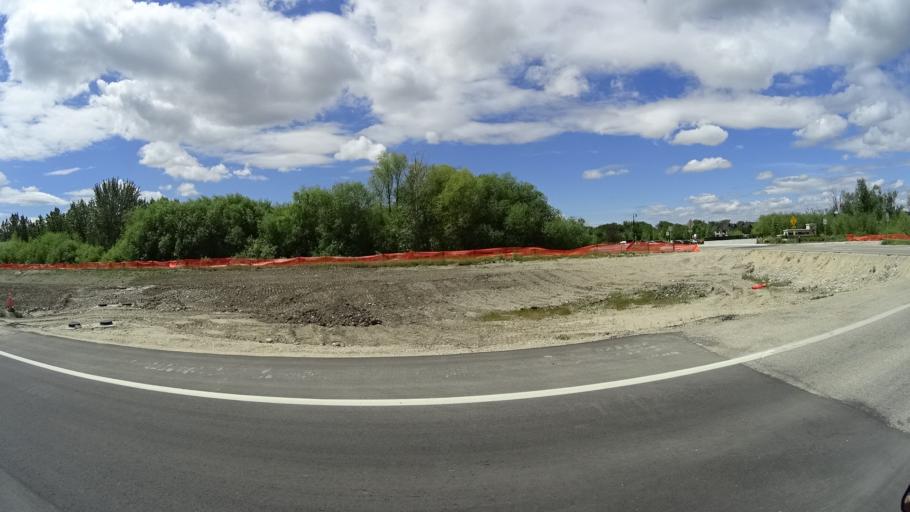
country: US
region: Idaho
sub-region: Ada County
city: Boise
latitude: 43.5736
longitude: -116.1391
